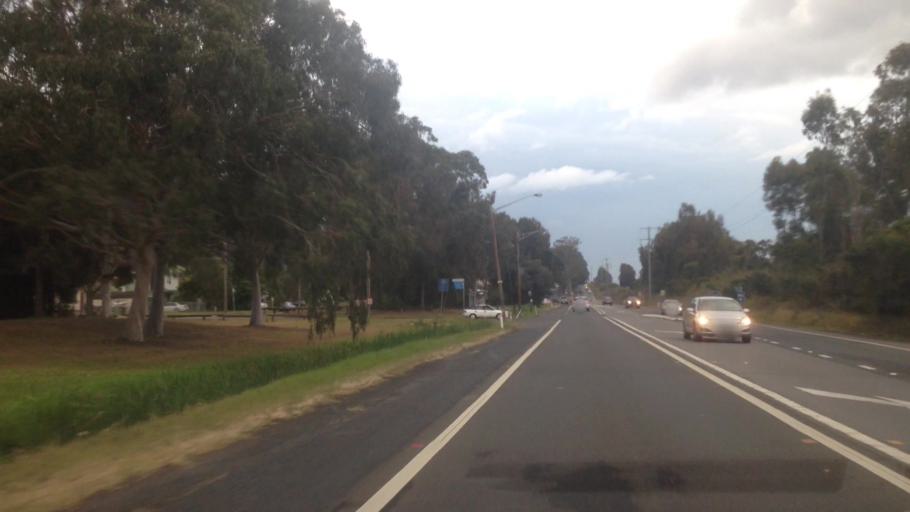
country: AU
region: New South Wales
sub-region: Wyong Shire
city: Chittaway Bay
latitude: -33.2773
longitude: 151.4282
